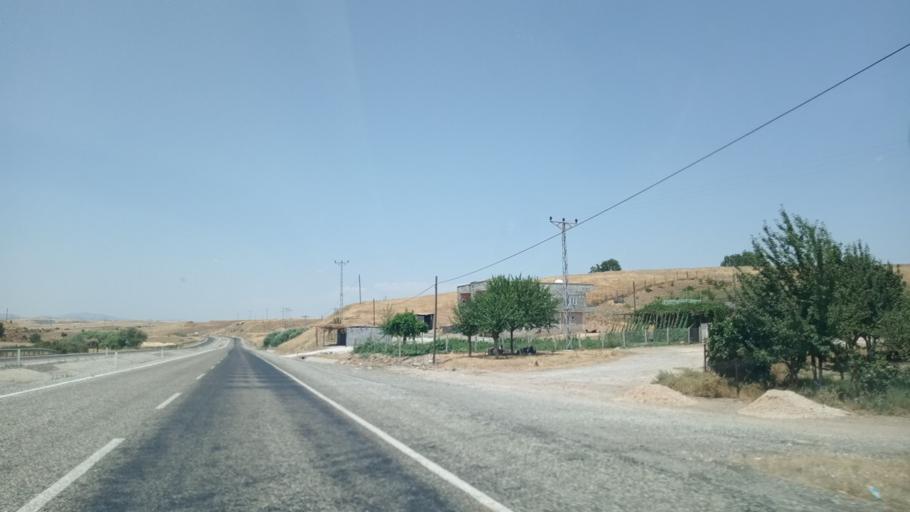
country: TR
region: Batman
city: Bekirhan
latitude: 38.1559
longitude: 41.3513
